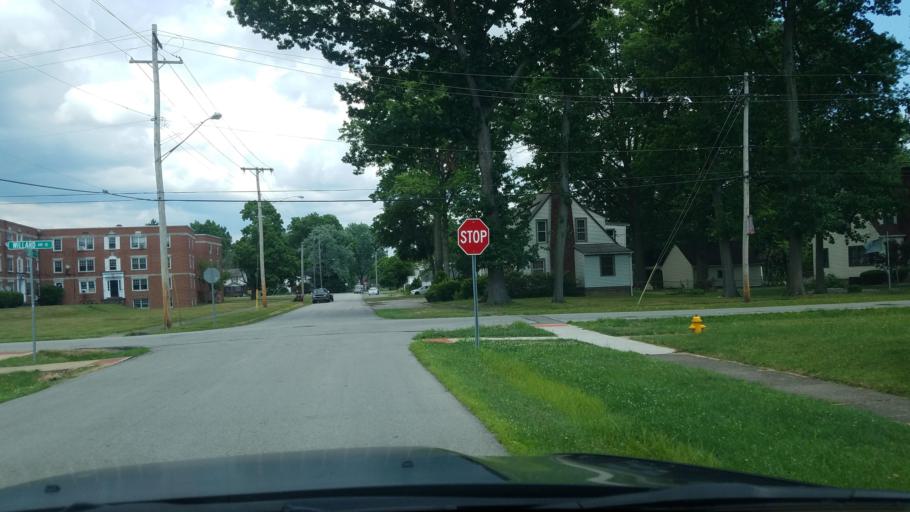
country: US
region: Ohio
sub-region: Trumbull County
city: Bolindale
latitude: 41.2345
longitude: -80.7884
